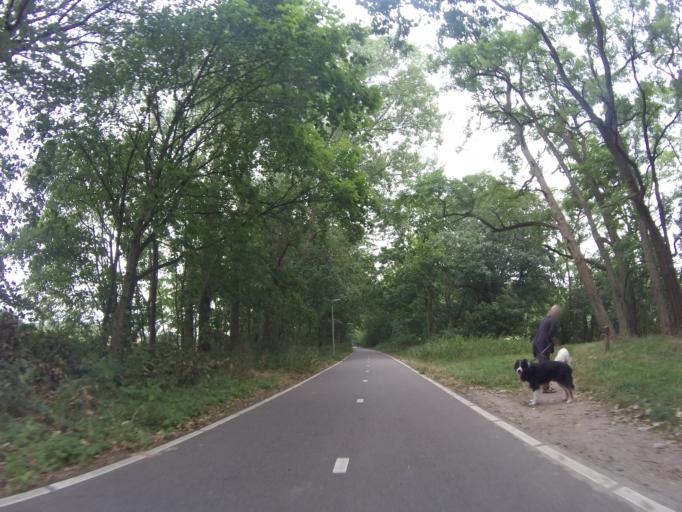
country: NL
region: North Holland
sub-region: Gemeente Hilversum
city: Hilversum
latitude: 52.2212
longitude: 5.2022
